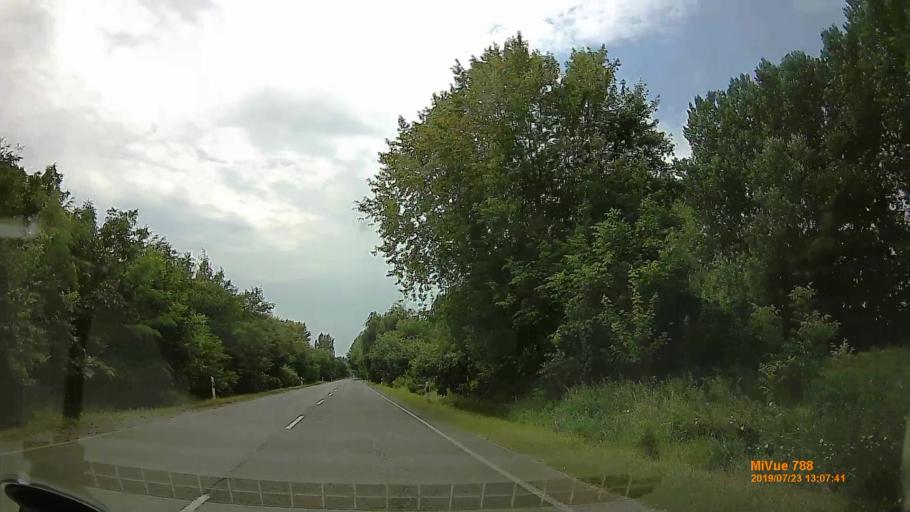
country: HU
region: Szabolcs-Szatmar-Bereg
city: Tiszavasvari
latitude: 47.9542
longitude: 21.3323
